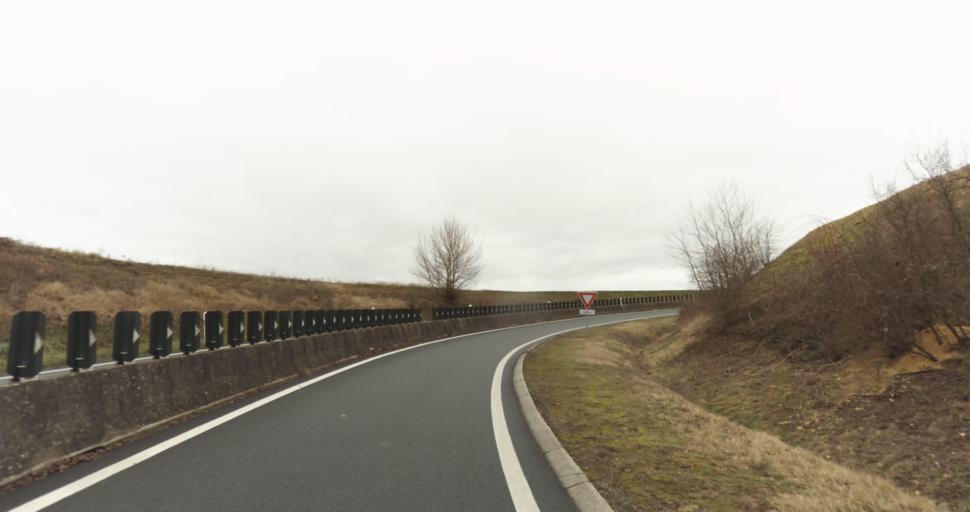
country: FR
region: Pays de la Loire
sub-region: Departement de Maine-et-Loire
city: Doue-la-Fontaine
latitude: 47.1978
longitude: -0.2452
